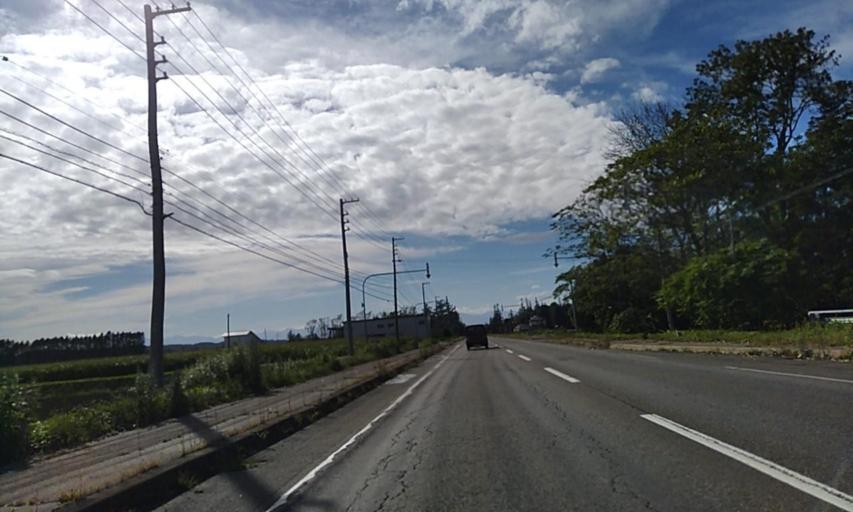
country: JP
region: Hokkaido
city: Obihiro
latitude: 42.9200
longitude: 143.3213
